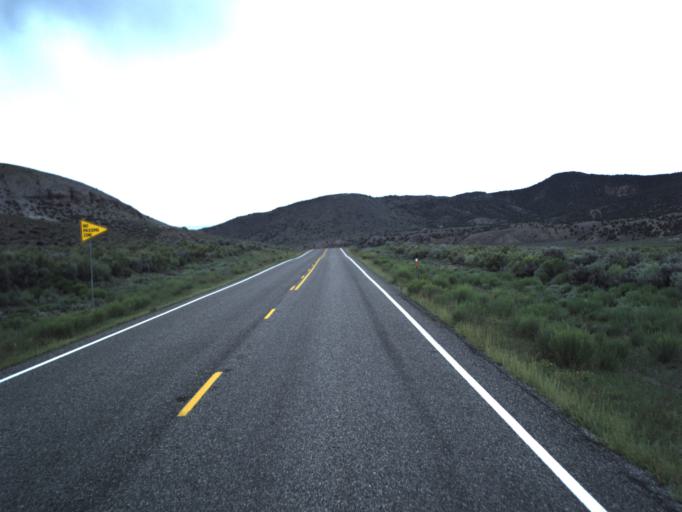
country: US
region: Utah
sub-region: Piute County
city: Junction
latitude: 38.1748
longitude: -112.0643
